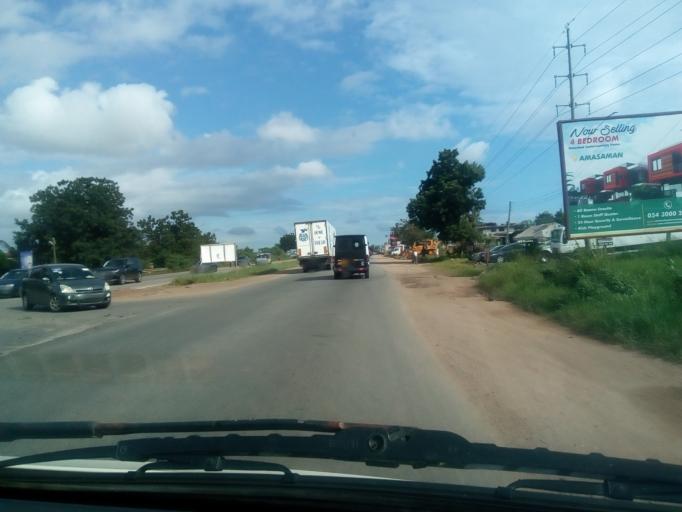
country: GH
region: Greater Accra
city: Achiaman
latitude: 5.7004
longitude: -0.2942
